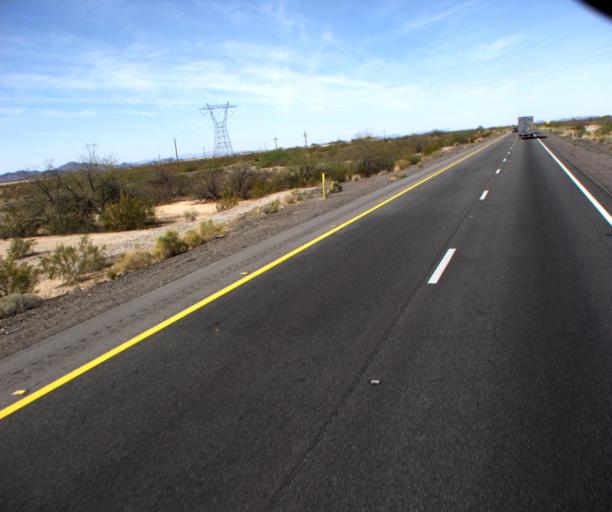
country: US
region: Arizona
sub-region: La Paz County
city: Salome
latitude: 33.5756
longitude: -113.3946
